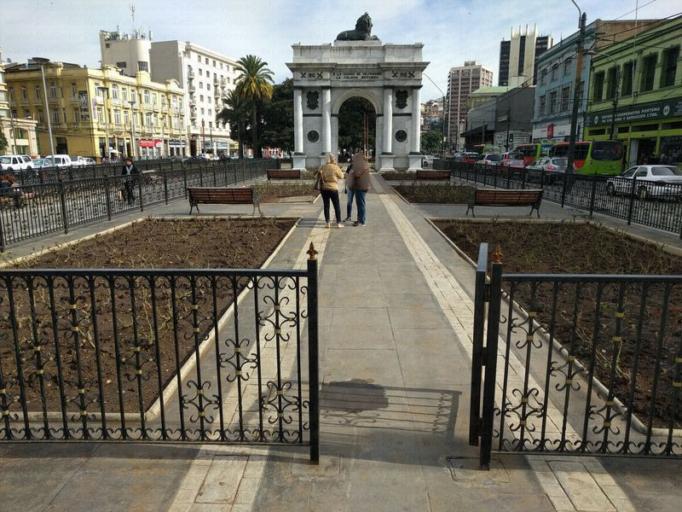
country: CL
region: Valparaiso
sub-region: Provincia de Valparaiso
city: Valparaiso
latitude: -33.0447
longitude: -71.6199
